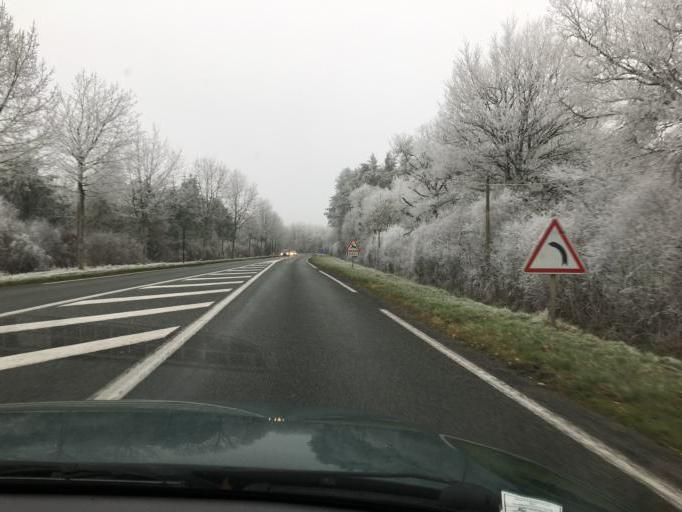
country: FR
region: Centre
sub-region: Departement du Loiret
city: La Ferte-Saint-Aubin
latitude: 47.7424
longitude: 1.9340
